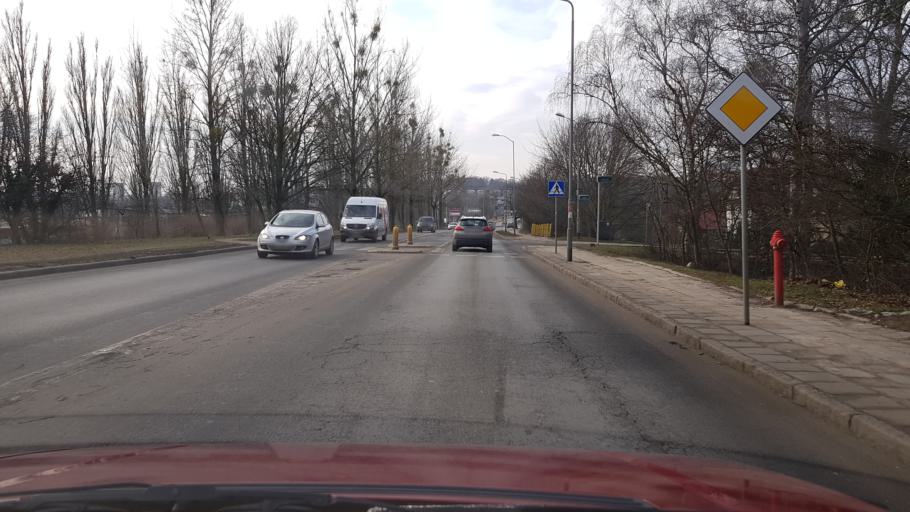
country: PL
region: West Pomeranian Voivodeship
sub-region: Szczecin
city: Szczecin
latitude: 53.4610
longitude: 14.5753
